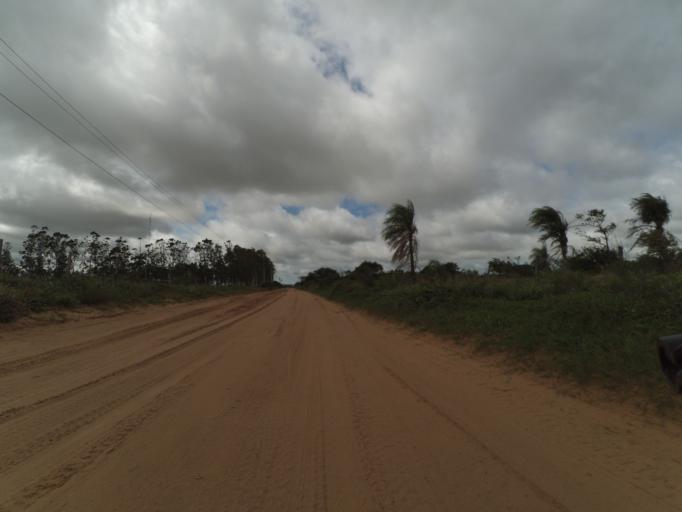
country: BO
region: Santa Cruz
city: Santa Cruz de la Sierra
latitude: -17.8957
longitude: -63.2415
